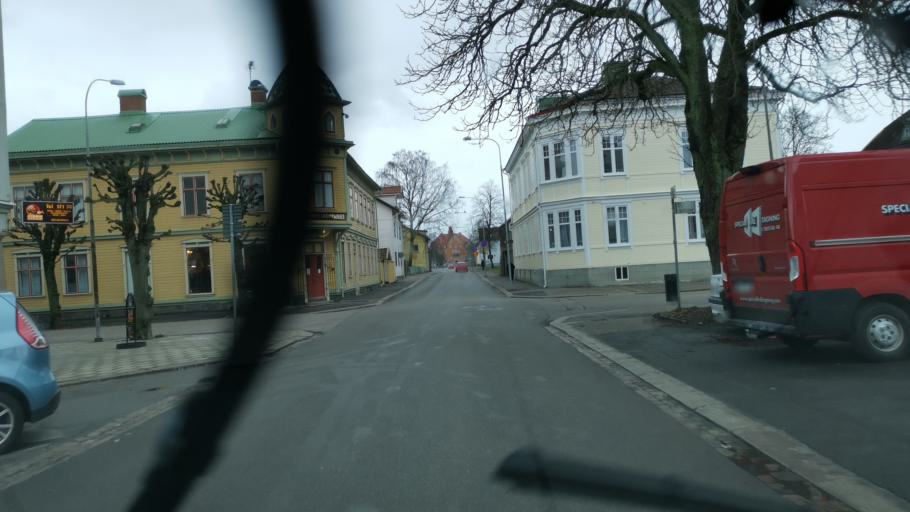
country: SE
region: Vaestra Goetaland
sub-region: Vanersborgs Kommun
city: Vanersborg
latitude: 58.3776
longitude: 12.3270
